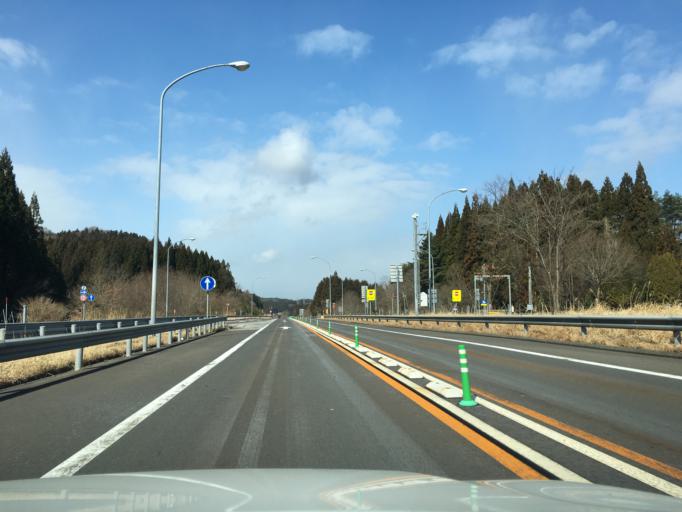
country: JP
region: Akita
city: Akita
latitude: 39.7502
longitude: 140.1505
